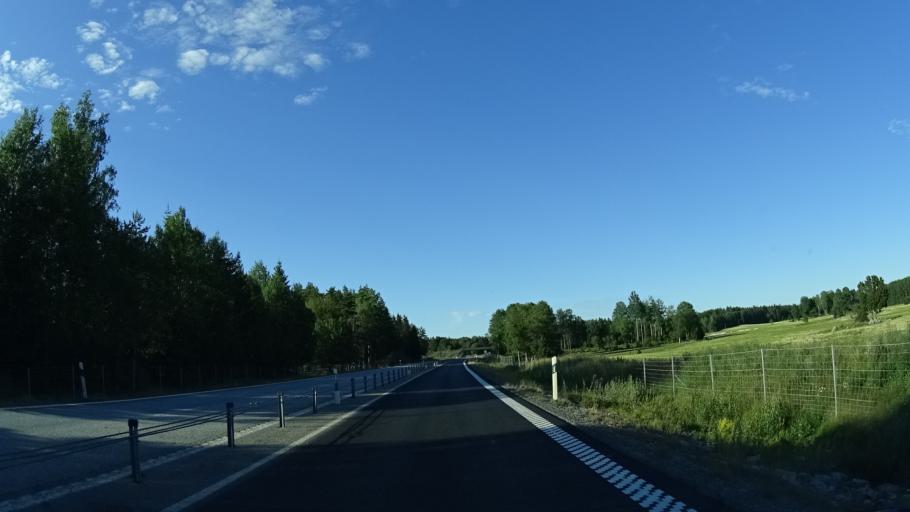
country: SE
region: Stockholm
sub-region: Osterakers Kommun
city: Akersberga
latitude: 59.6058
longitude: 18.2781
